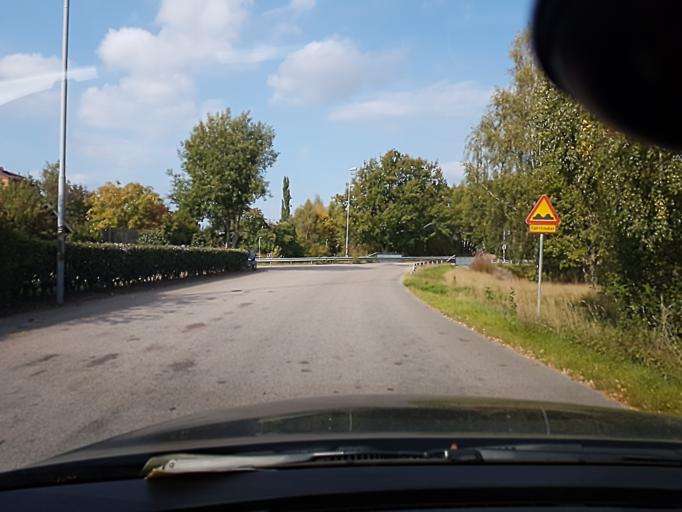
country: SE
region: Kronoberg
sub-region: Vaxjo Kommun
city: Vaexjoe
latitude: 56.8464
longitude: 14.8201
